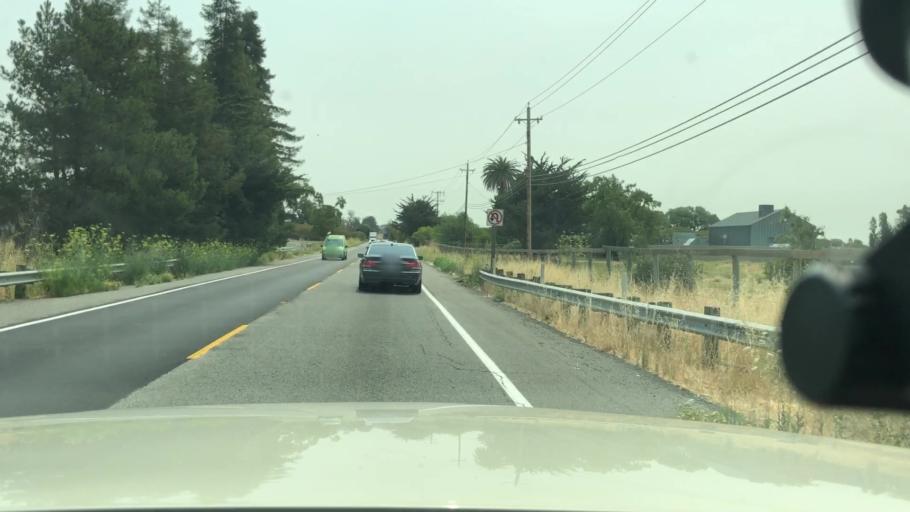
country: US
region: California
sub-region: Sonoma County
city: Petaluma
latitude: 38.2288
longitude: -122.5799
